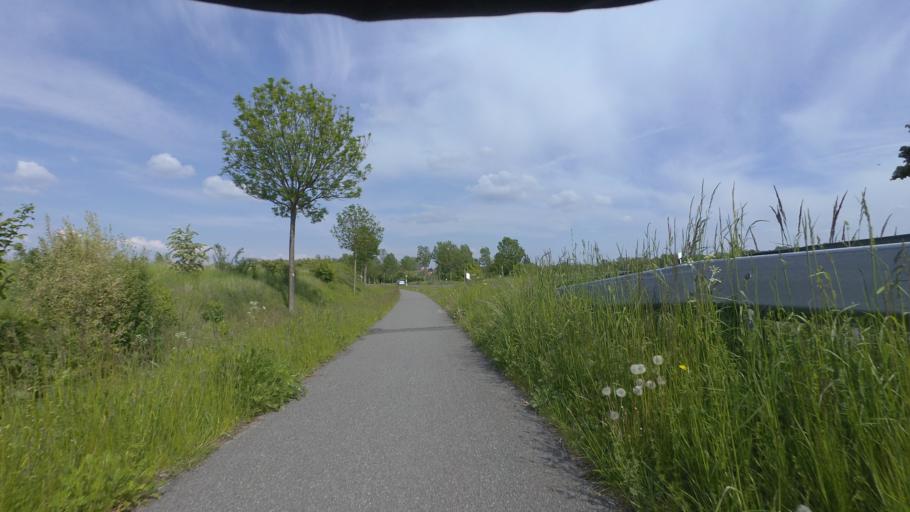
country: DE
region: Saxony-Anhalt
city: Hotensleben
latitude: 52.1225
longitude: 11.0053
